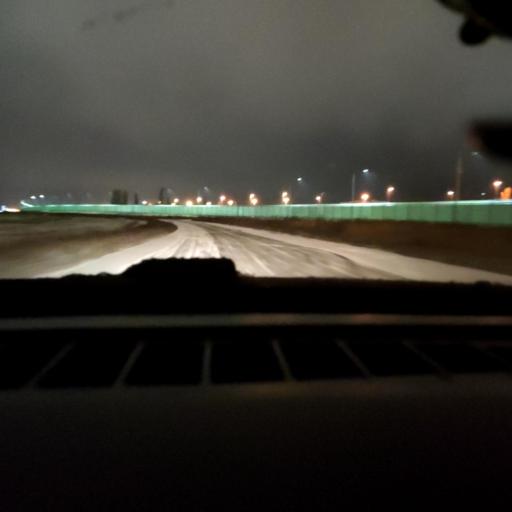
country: RU
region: Voronezj
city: Novaya Usman'
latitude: 51.6513
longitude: 39.3044
